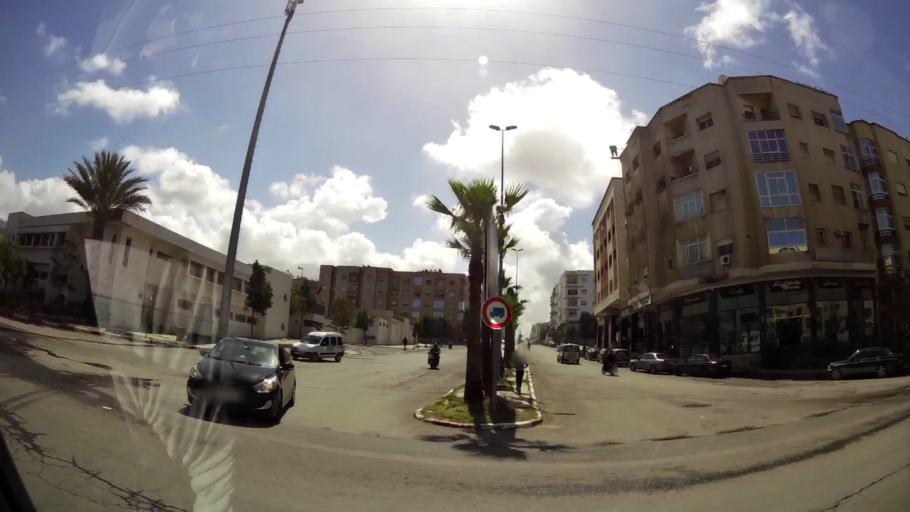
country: MA
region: Grand Casablanca
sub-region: Mediouna
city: Tit Mellil
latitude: 33.6217
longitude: -7.4881
